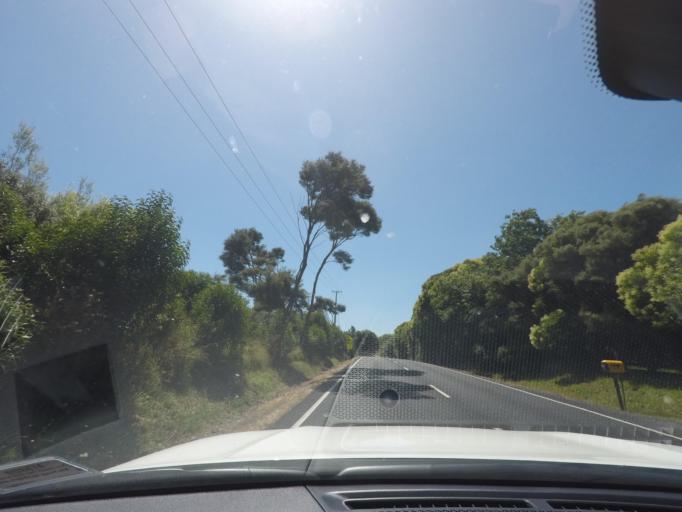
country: NZ
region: Auckland
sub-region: Auckland
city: Parakai
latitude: -36.6449
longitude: 174.3965
